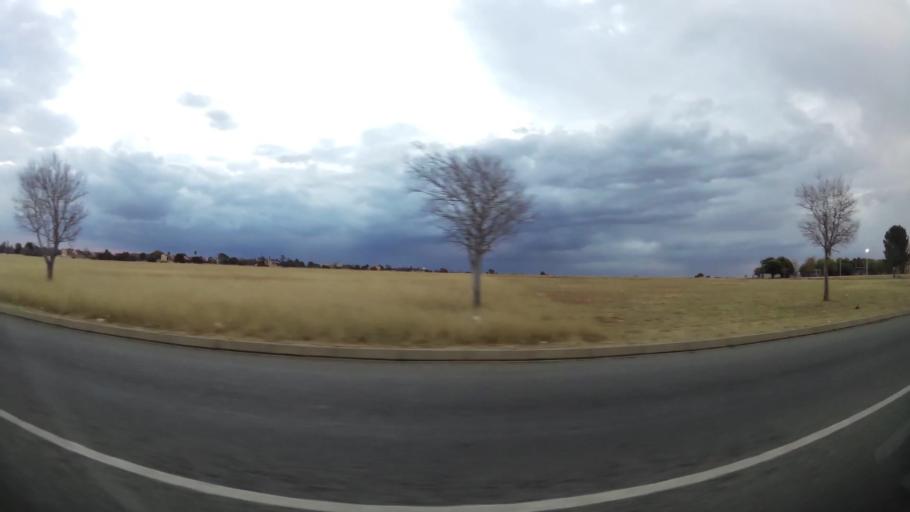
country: ZA
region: Orange Free State
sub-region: Lejweleputswa District Municipality
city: Welkom
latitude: -27.9553
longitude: 26.7549
